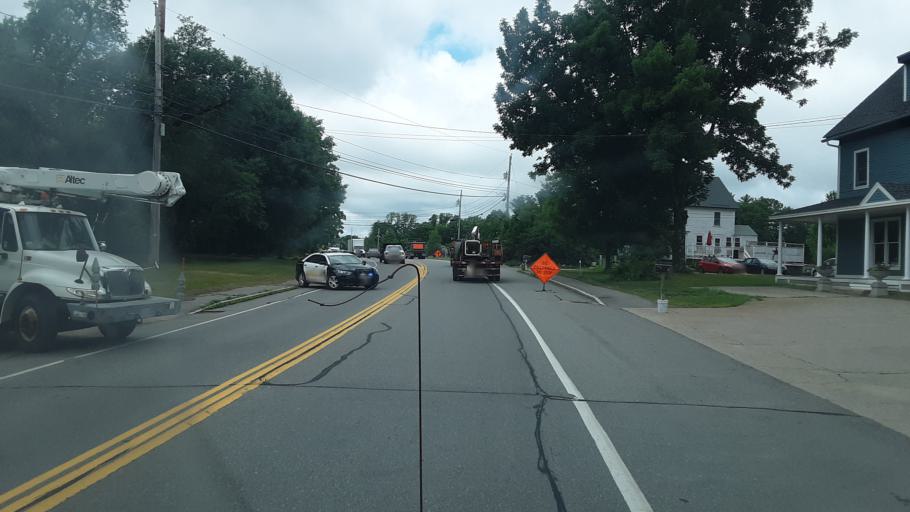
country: US
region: New Hampshire
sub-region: Rockingham County
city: Northwood
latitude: 43.1919
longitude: -71.1461
